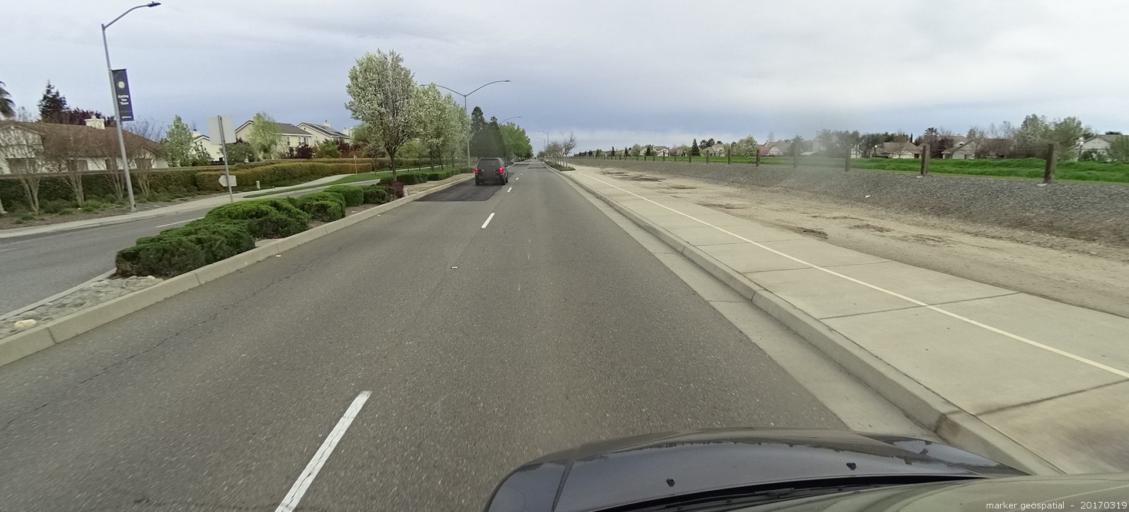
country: US
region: California
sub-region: Sacramento County
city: Elverta
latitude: 38.6746
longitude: -121.5077
